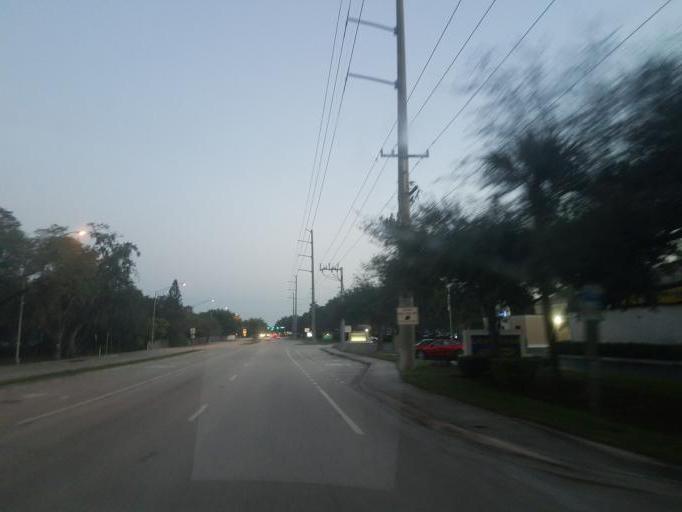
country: US
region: Florida
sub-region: Sarasota County
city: Lake Sarasota
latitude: 27.3027
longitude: -82.4515
